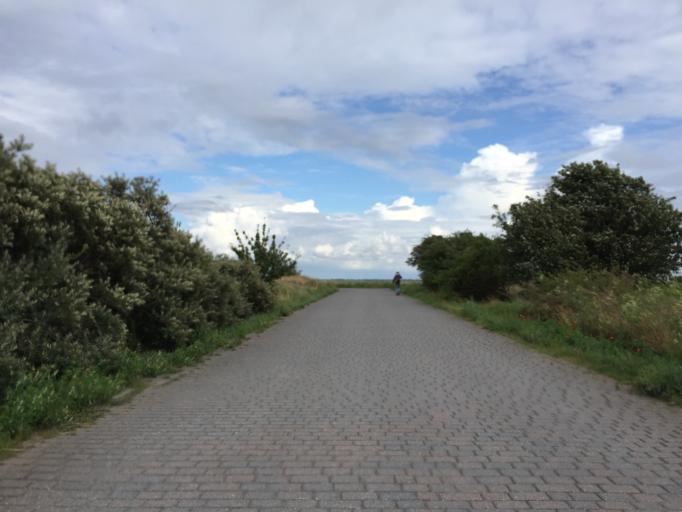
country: DE
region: Mecklenburg-Vorpommern
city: Hiddensee
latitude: 54.5604
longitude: 13.1073
